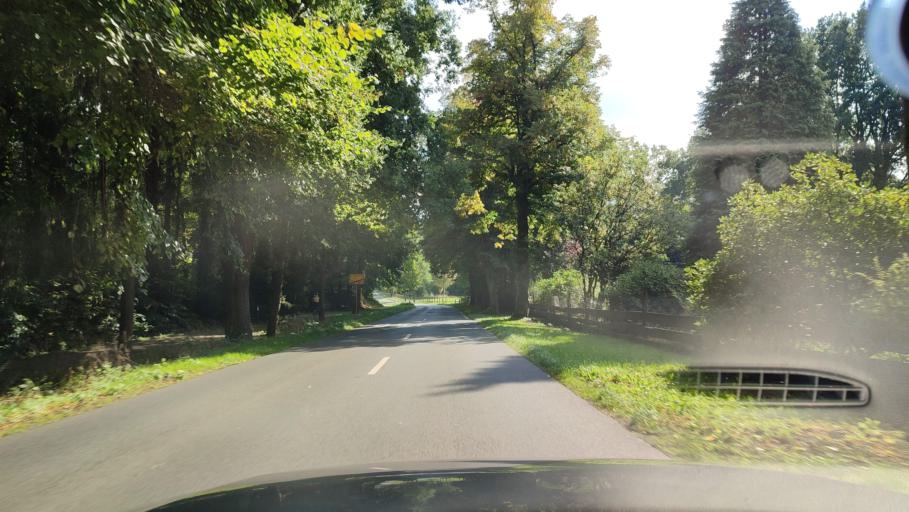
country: DE
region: Lower Saxony
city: Bad Fallingbostel
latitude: 52.8730
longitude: 9.6663
